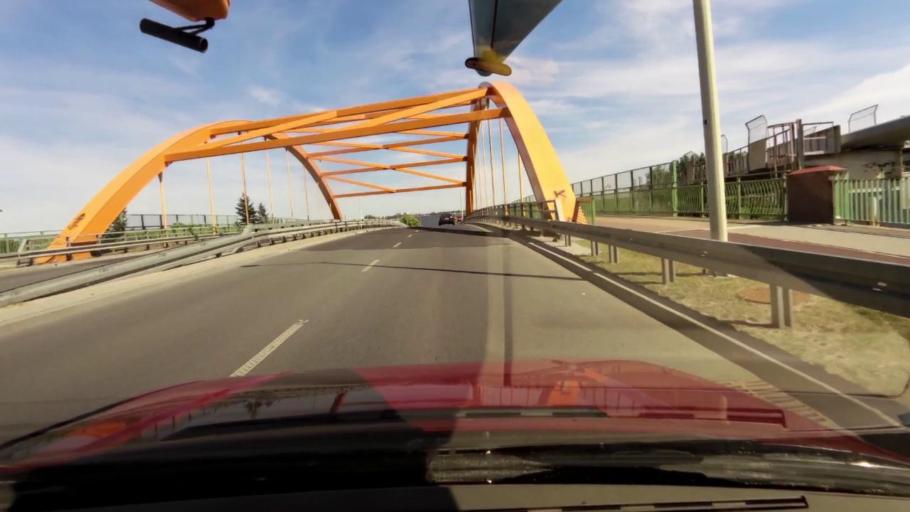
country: PL
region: Pomeranian Voivodeship
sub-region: Powiat slupski
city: Kobylnica
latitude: 54.4551
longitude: 17.0102
